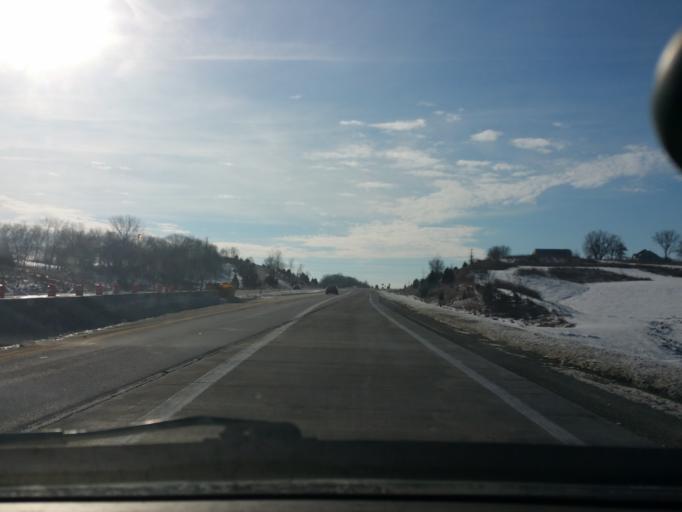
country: US
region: Iowa
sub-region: Warren County
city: Norwalk
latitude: 41.4198
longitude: -93.7806
